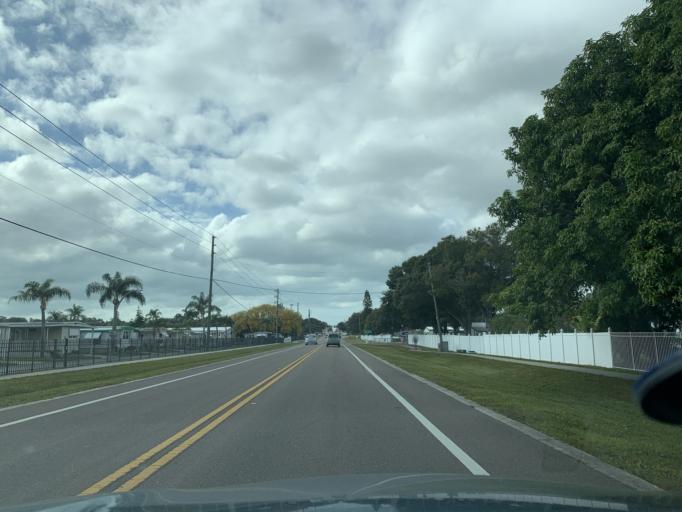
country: US
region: Florida
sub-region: Pinellas County
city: Ridgecrest
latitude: 27.8801
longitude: -82.7913
